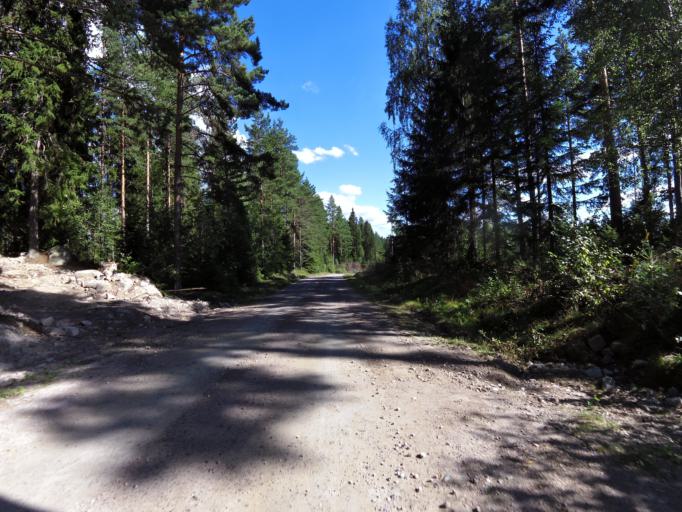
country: SE
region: Dalarna
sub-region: Faluns Kommun
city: Svardsjo
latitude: 60.6631
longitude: 15.8555
